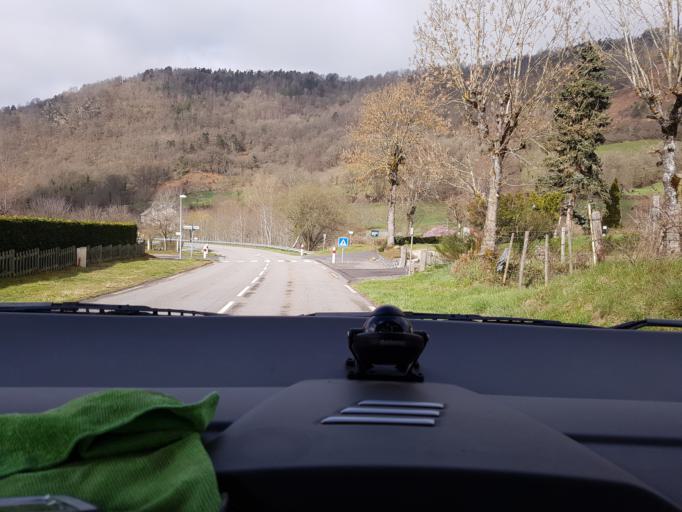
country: FR
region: Auvergne
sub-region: Departement du Cantal
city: Neuveglise
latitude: 44.8932
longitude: 3.0012
